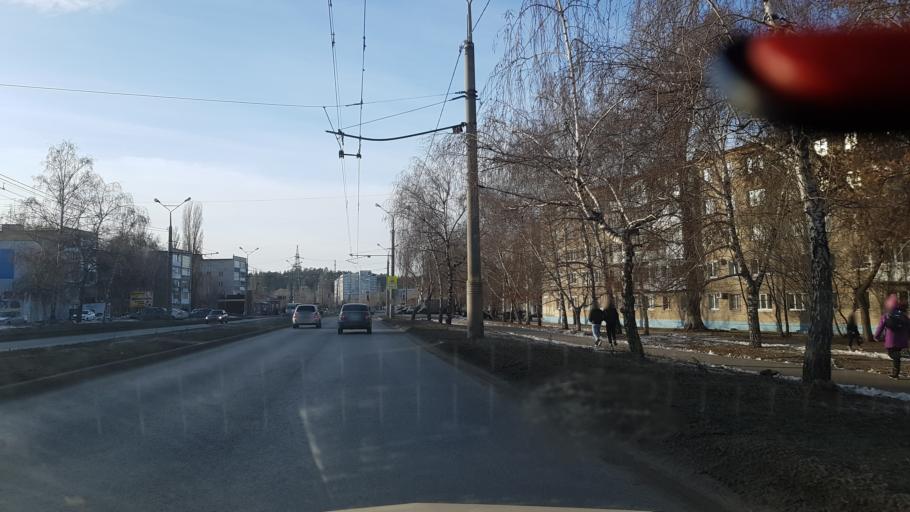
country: RU
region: Samara
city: Tol'yatti
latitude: 53.5294
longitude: 49.4007
